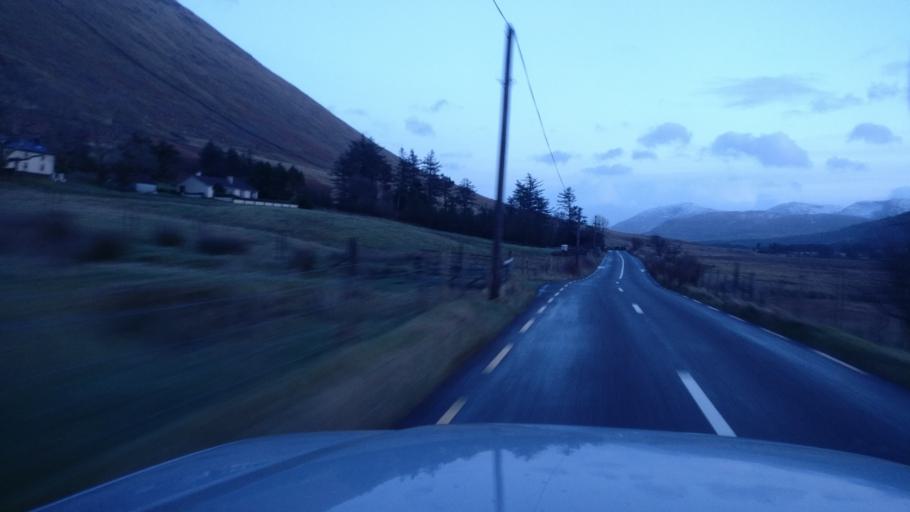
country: IE
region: Connaught
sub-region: Maigh Eo
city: Westport
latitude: 53.5682
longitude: -9.6544
